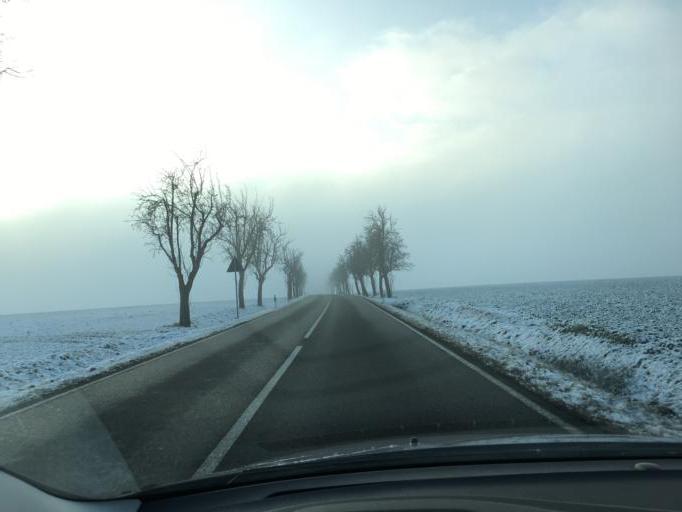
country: DE
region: Saxony
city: Narsdorf
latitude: 51.0245
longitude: 12.7287
